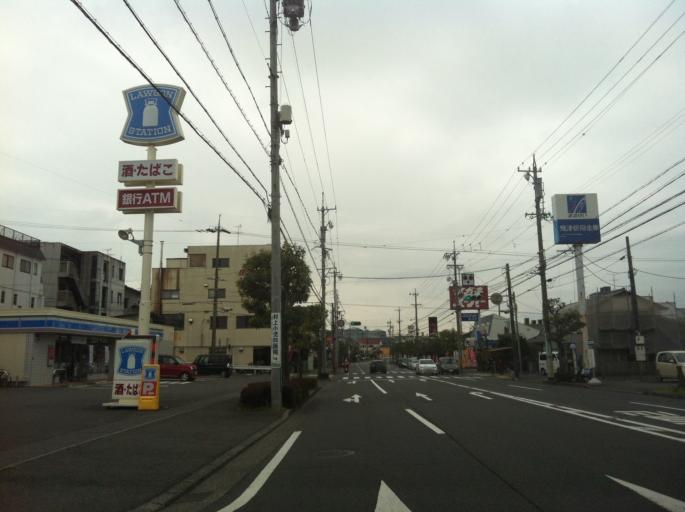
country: JP
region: Shizuoka
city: Shizuoka-shi
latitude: 35.0055
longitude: 138.4526
